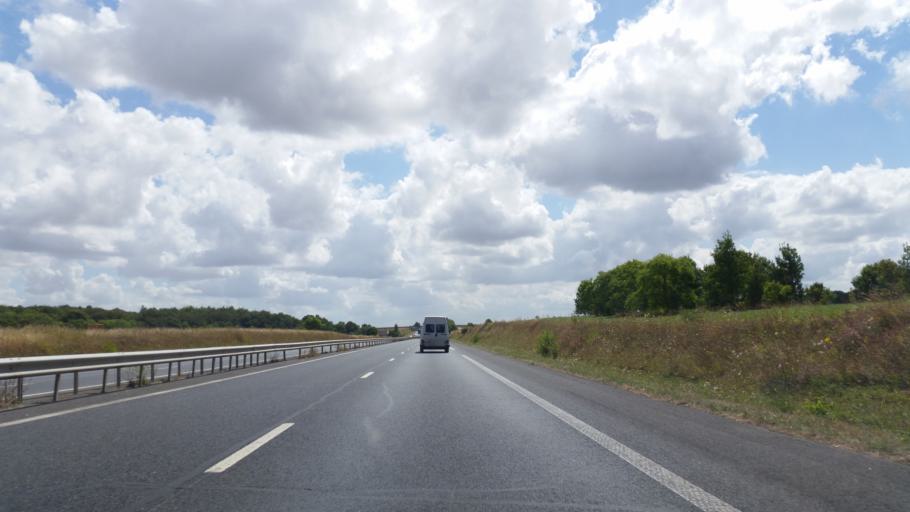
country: FR
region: Lower Normandy
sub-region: Departement du Calvados
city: Potigny
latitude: 48.9985
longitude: -0.2566
